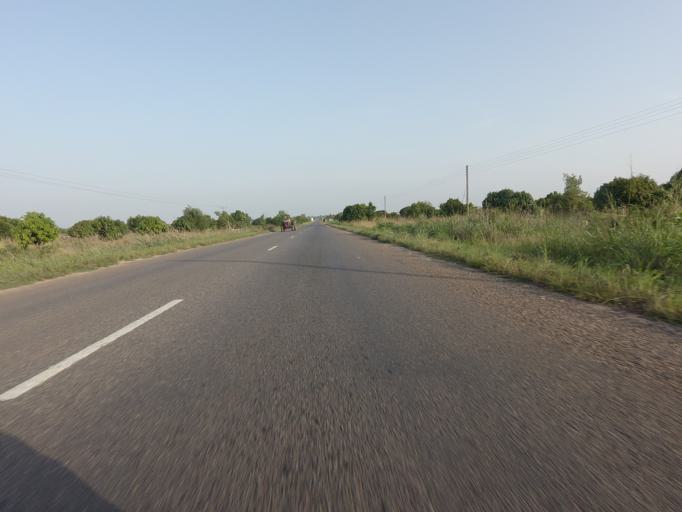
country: GH
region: Volta
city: Anloga
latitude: 6.0110
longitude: 0.6678
